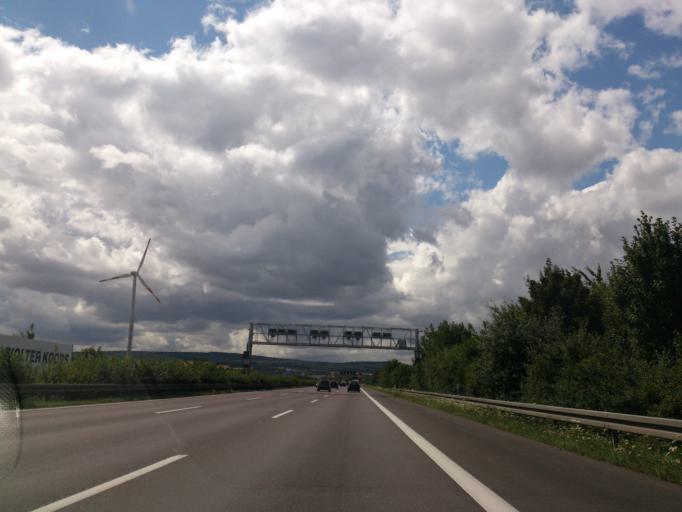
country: DE
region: Lower Saxony
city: Haste
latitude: 52.3538
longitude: 9.4275
